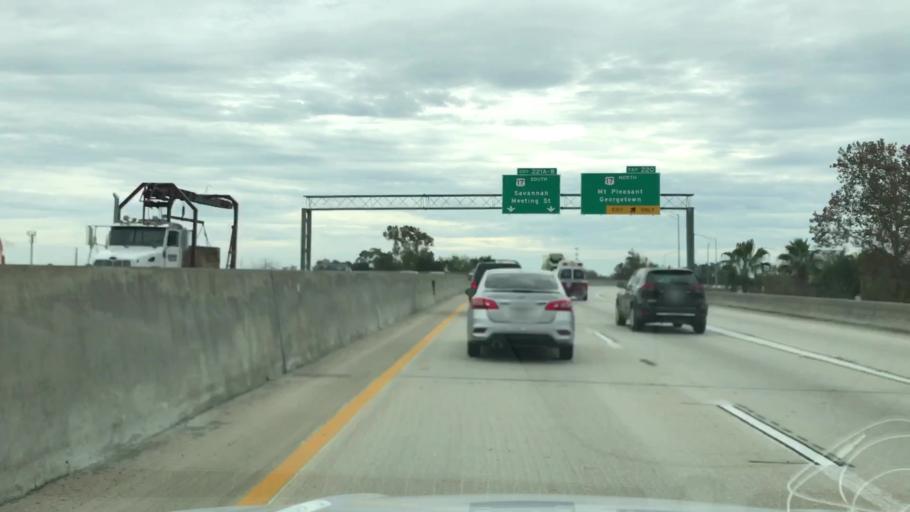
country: US
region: South Carolina
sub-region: Charleston County
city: Charleston
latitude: 32.8113
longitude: -79.9513
